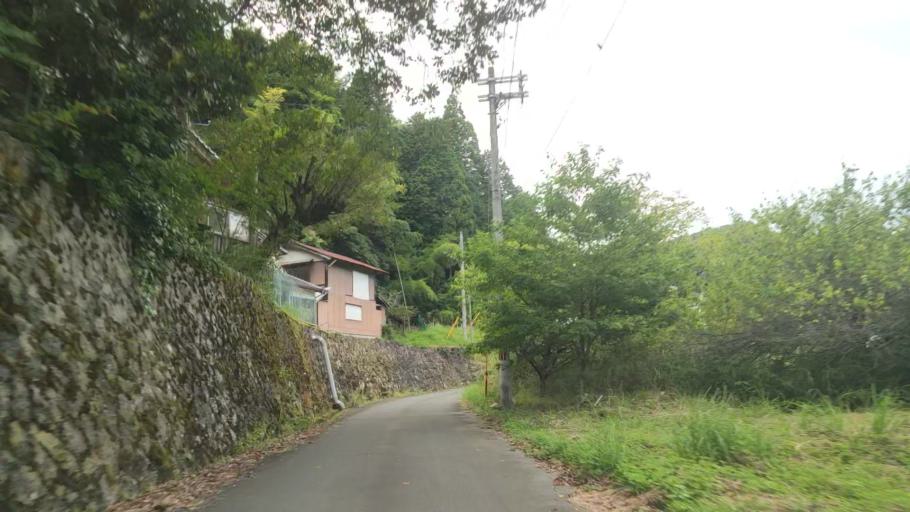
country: JP
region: Hyogo
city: Toyooka
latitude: 35.5988
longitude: 134.8816
